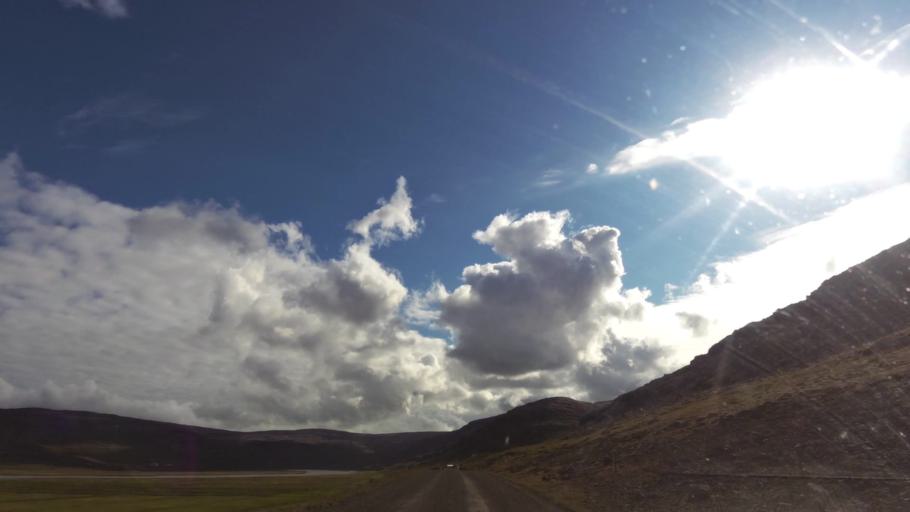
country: IS
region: West
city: Olafsvik
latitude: 65.5810
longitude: -24.1428
